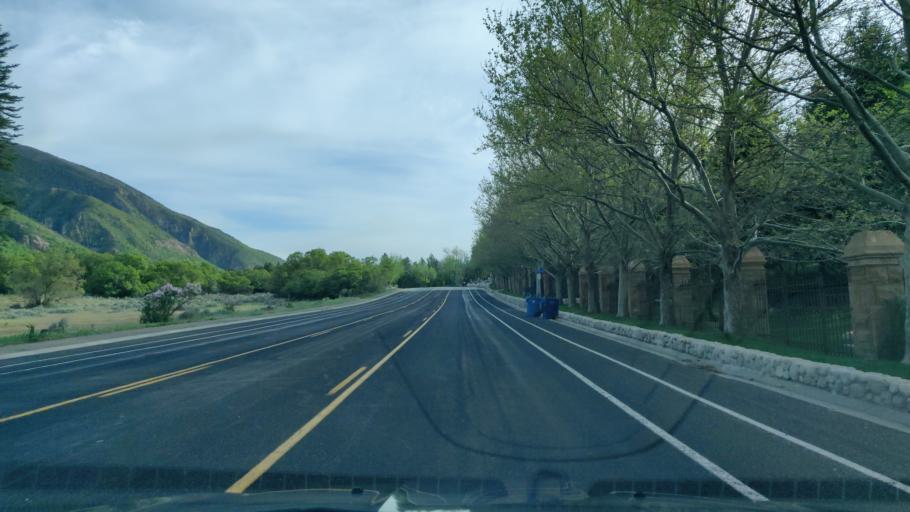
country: US
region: Utah
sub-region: Salt Lake County
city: Granite
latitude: 40.5563
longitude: -111.8019
